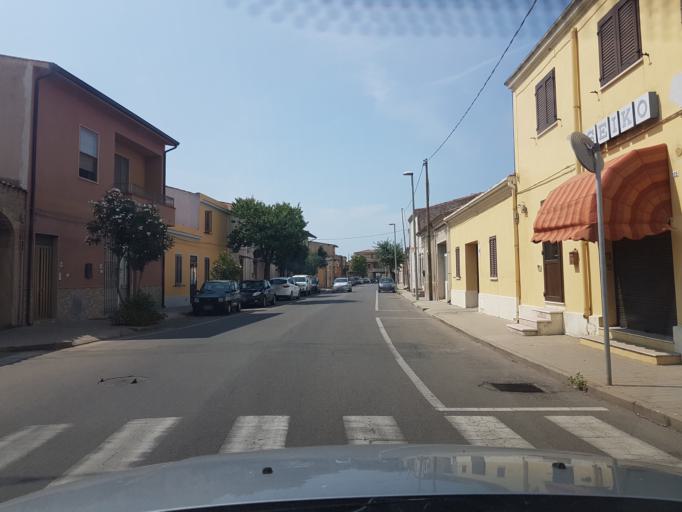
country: IT
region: Sardinia
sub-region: Provincia di Oristano
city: Cabras
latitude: 39.9261
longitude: 8.5349
